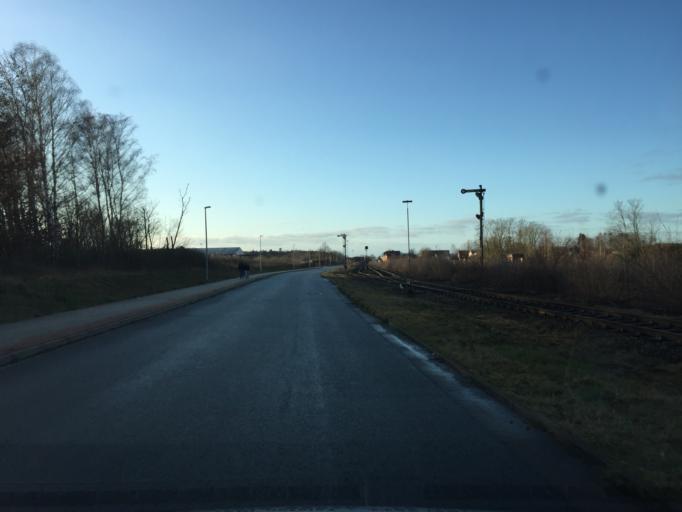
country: DE
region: Lower Saxony
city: Sulingen
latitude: 52.6906
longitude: 8.8140
